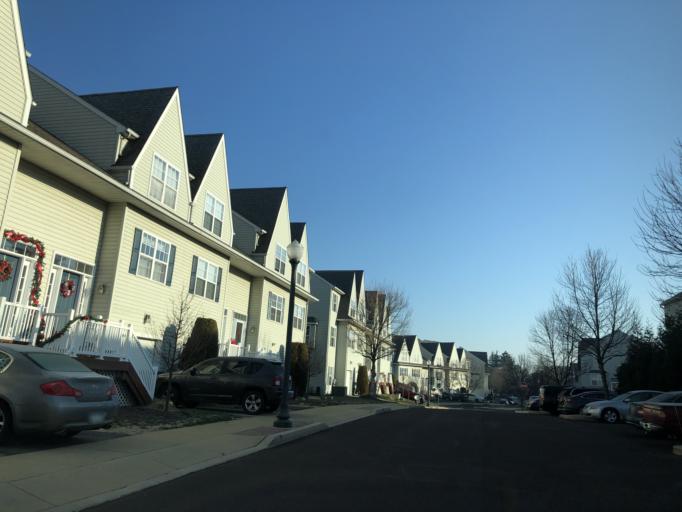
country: US
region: Pennsylvania
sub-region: Chester County
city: Downingtown
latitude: 40.0041
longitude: -75.7005
